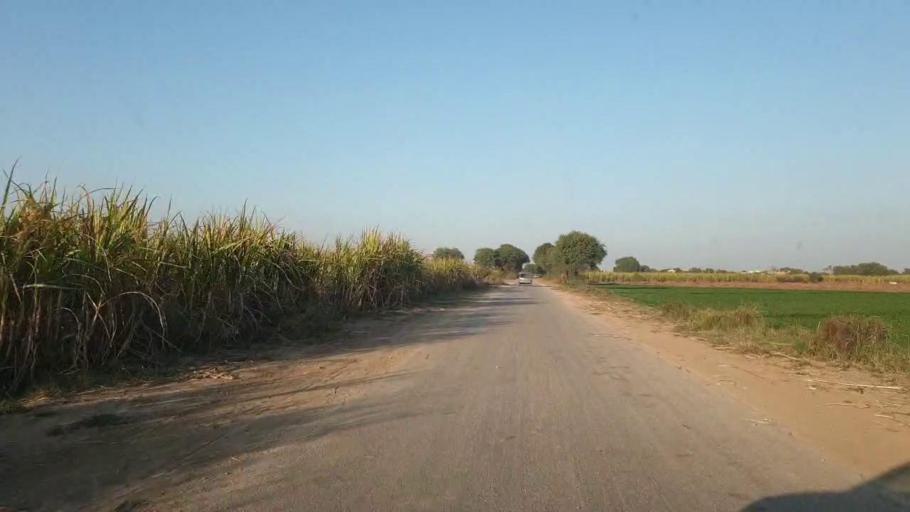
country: PK
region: Sindh
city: Chambar
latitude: 25.3626
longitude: 68.7404
